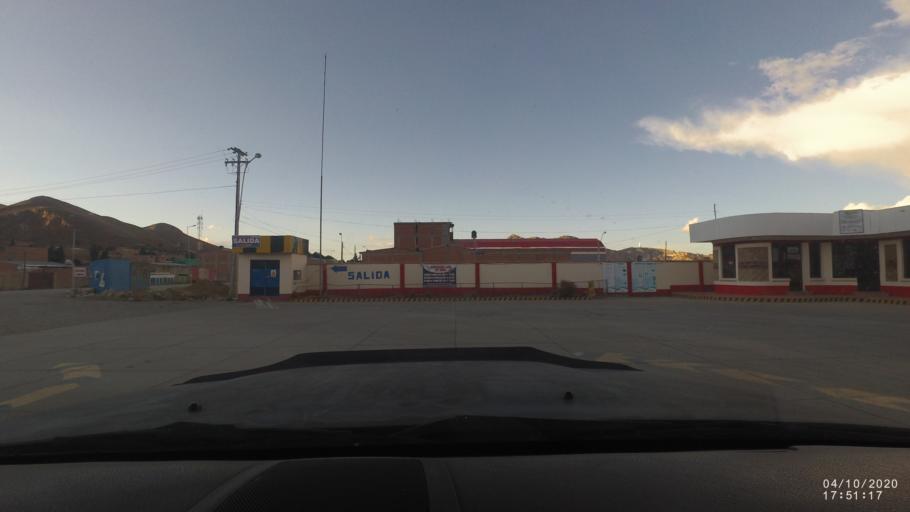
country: BO
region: Oruro
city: Oruro
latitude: -18.0015
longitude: -67.1355
